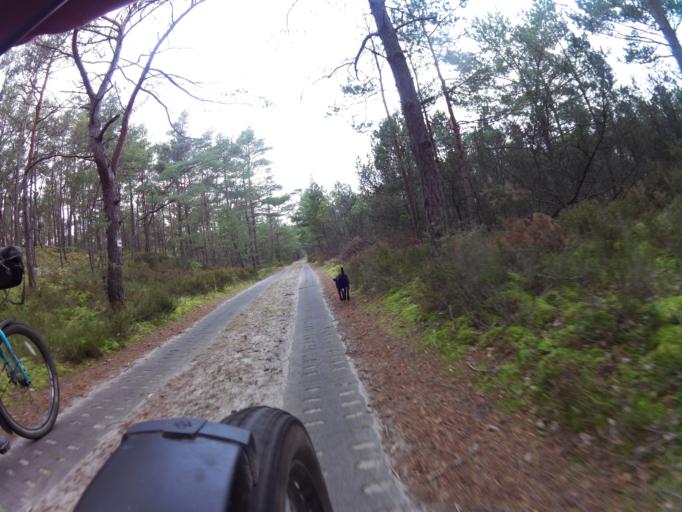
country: PL
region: Pomeranian Voivodeship
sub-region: Powiat pucki
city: Hel
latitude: 54.6235
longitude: 18.8181
